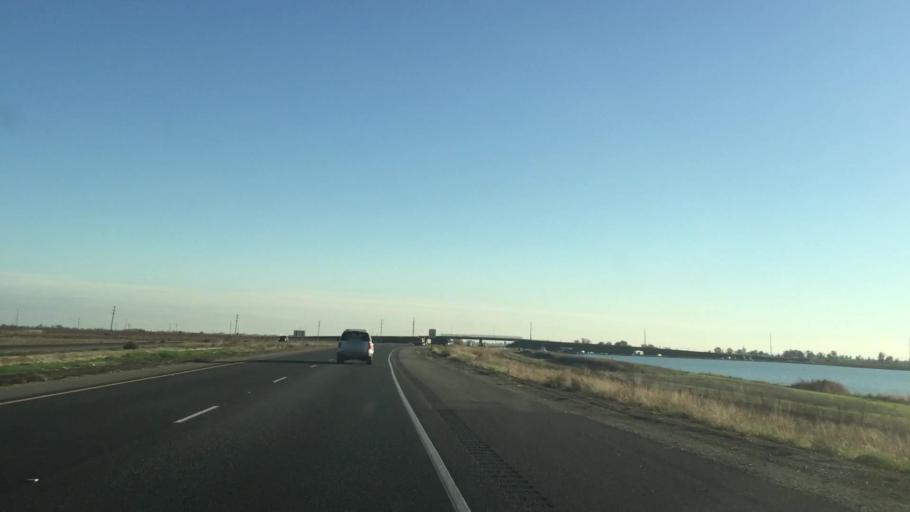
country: US
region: California
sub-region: Yuba County
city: Plumas Lake
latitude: 38.9025
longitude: -121.5475
